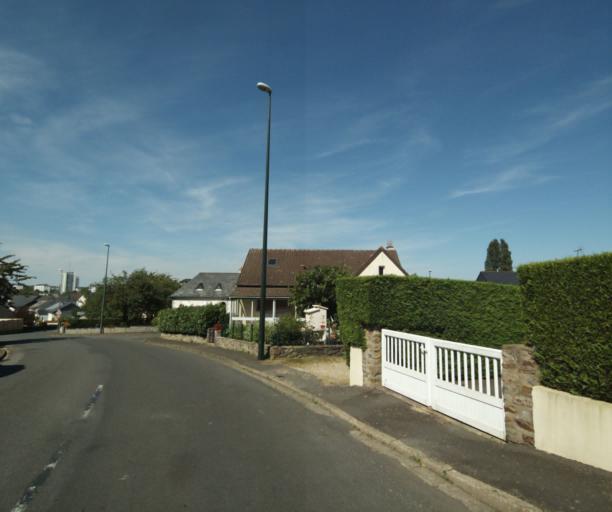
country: FR
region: Pays de la Loire
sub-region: Departement de la Mayenne
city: Laval
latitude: 48.0590
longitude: -0.7895
